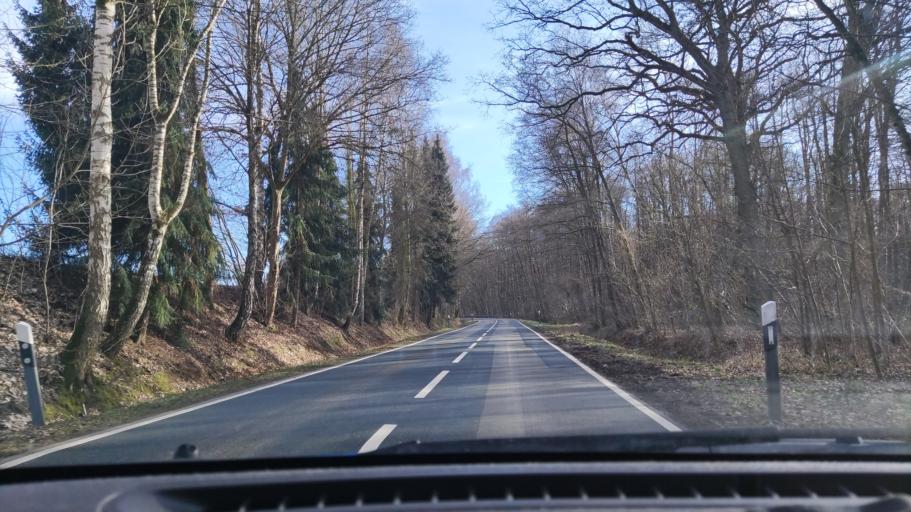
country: DE
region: Lower Saxony
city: Thomasburg
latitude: 53.2278
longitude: 10.6637
